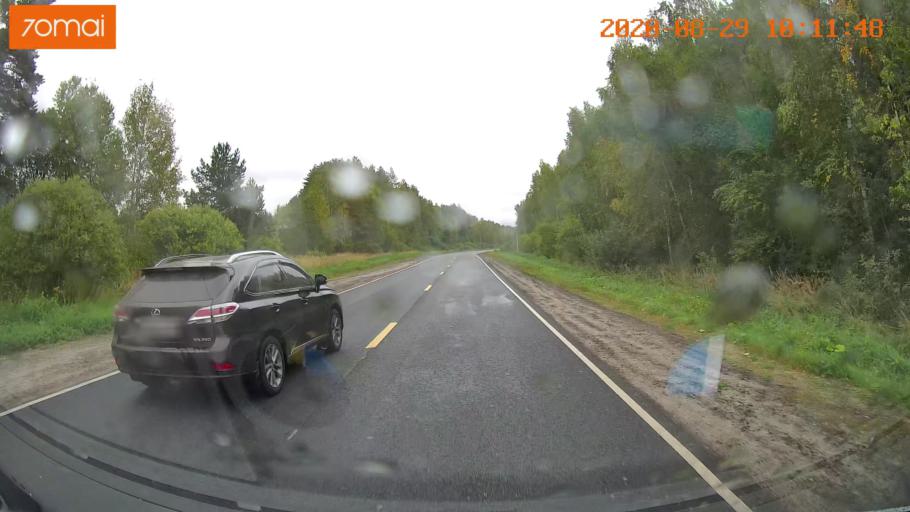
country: RU
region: Ivanovo
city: Kuznechikha
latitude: 57.3746
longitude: 42.6930
